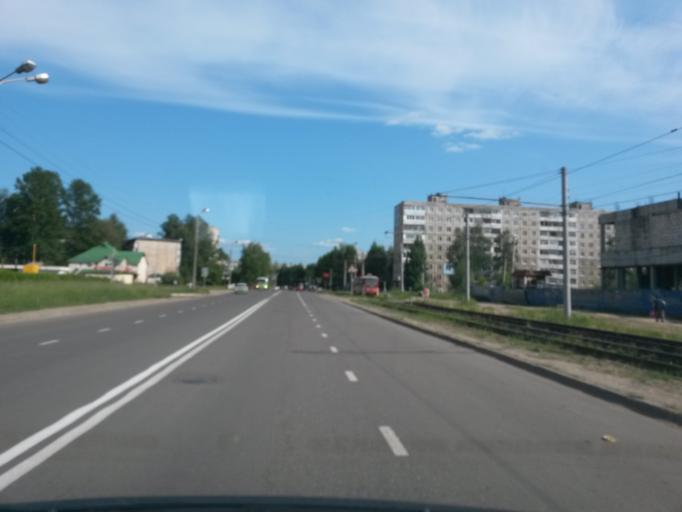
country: RU
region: Jaroslavl
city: Yaroslavl
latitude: 57.6853
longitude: 39.7676
